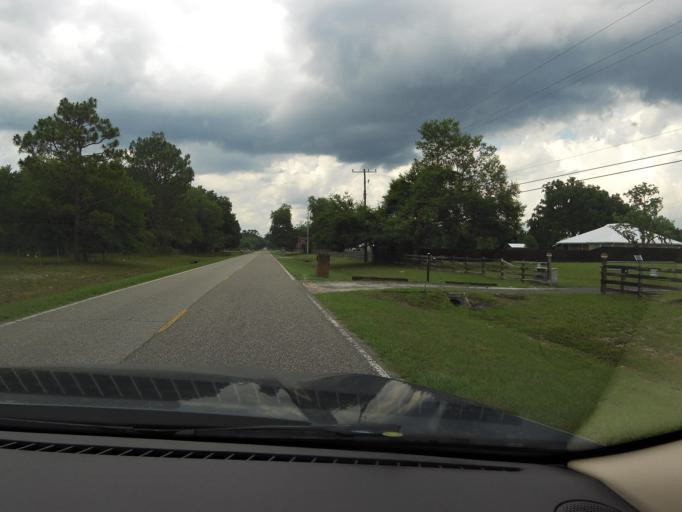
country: US
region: Florida
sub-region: Duval County
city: Baldwin
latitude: 30.3309
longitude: -81.8694
